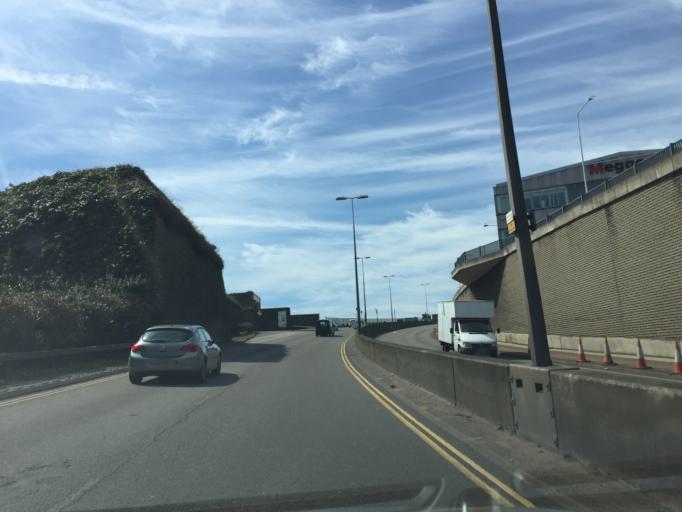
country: GB
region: England
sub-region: Kent
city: Dover
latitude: 51.1162
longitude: 1.3070
